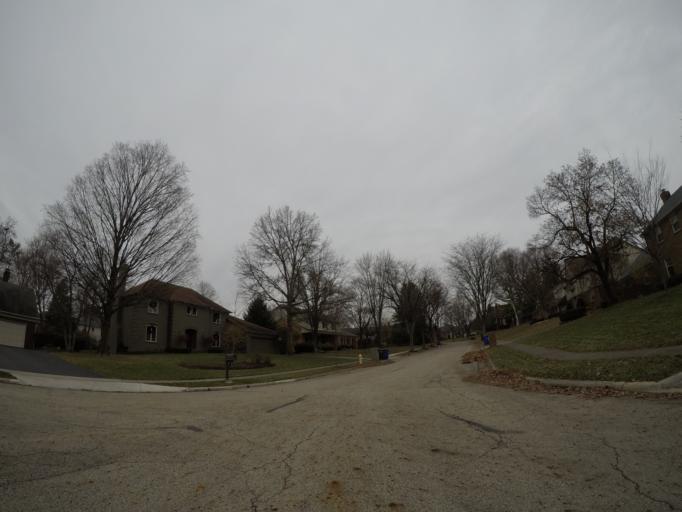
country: US
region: Ohio
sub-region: Franklin County
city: Dublin
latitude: 40.0503
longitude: -83.0871
